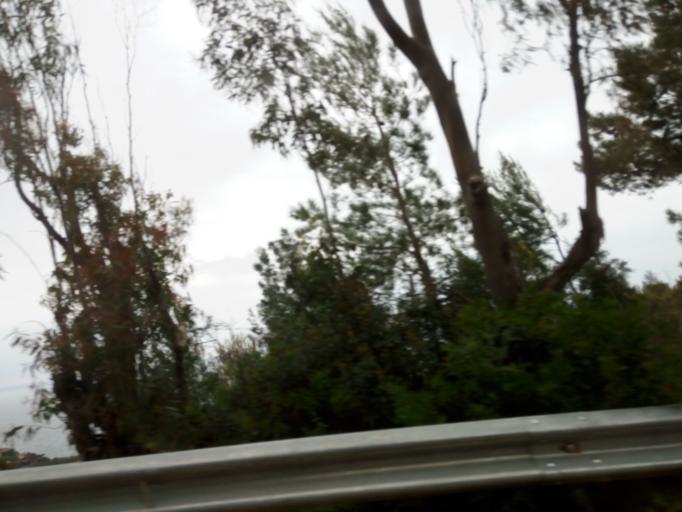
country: DZ
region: Tipaza
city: Tipasa
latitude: 36.5887
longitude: 2.5518
